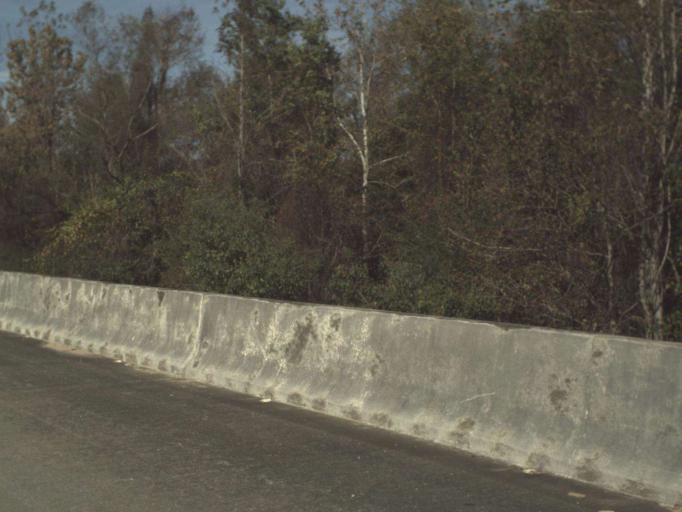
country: US
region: Florida
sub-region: Escambia County
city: Century
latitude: 30.9684
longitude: -87.2384
